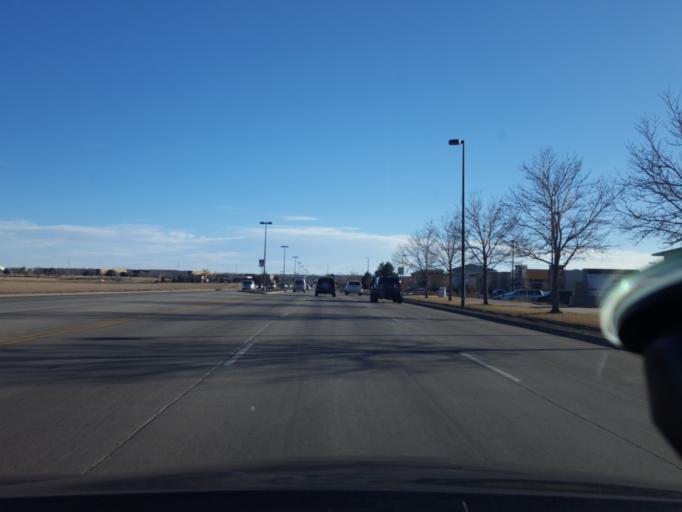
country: US
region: Colorado
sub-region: Adams County
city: Aurora
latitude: 39.7689
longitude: -104.7723
